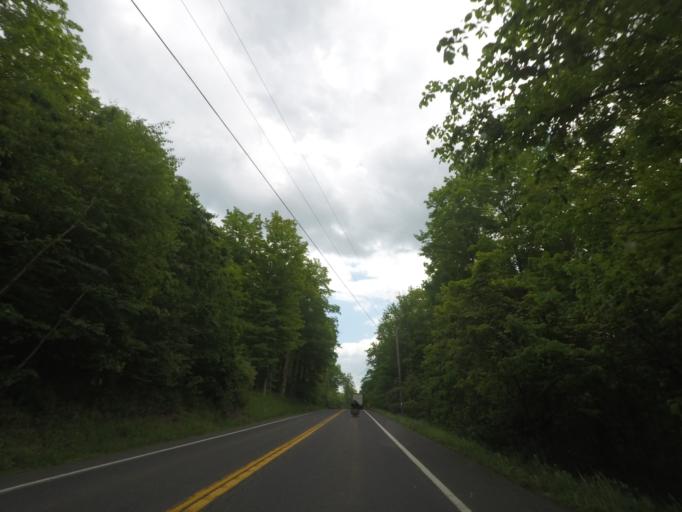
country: US
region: New York
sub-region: Dutchess County
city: Pine Plains
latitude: 42.0696
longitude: -73.6678
